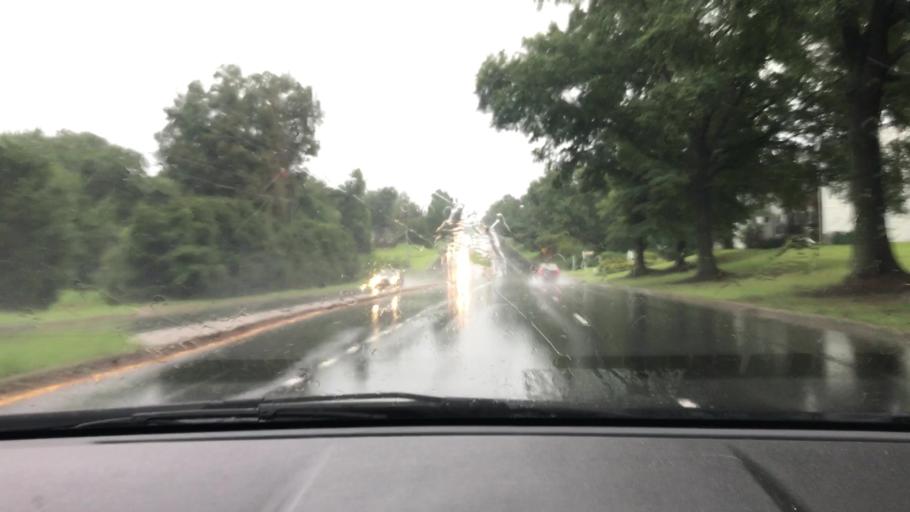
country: US
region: Virginia
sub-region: Henrico County
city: Laurel
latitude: 37.6489
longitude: -77.5578
